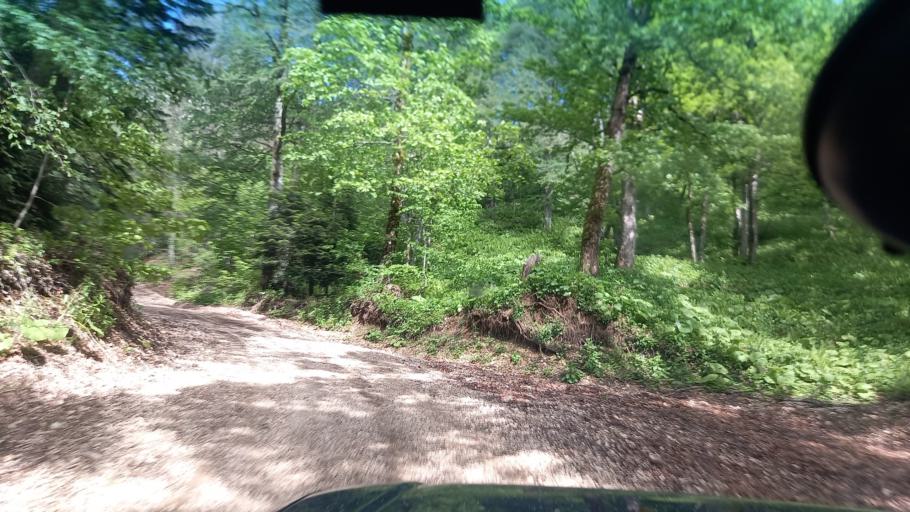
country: RU
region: Krasnodarskiy
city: Neftegorsk
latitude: 44.0129
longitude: 39.8548
